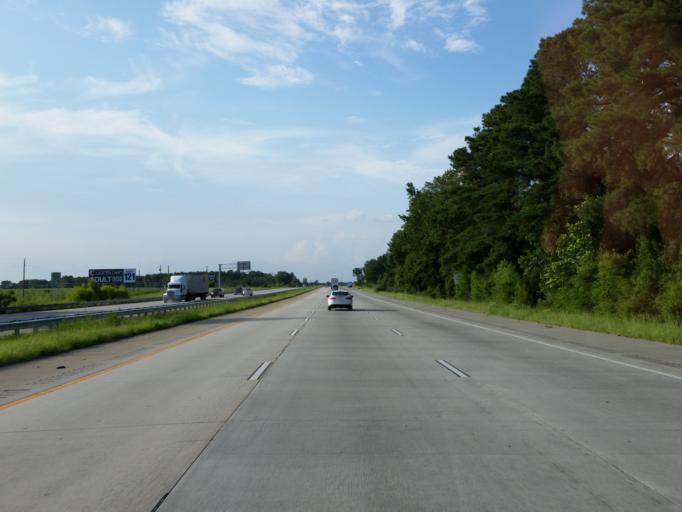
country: US
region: Georgia
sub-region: Dooly County
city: Unadilla
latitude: 32.1996
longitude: -83.7468
